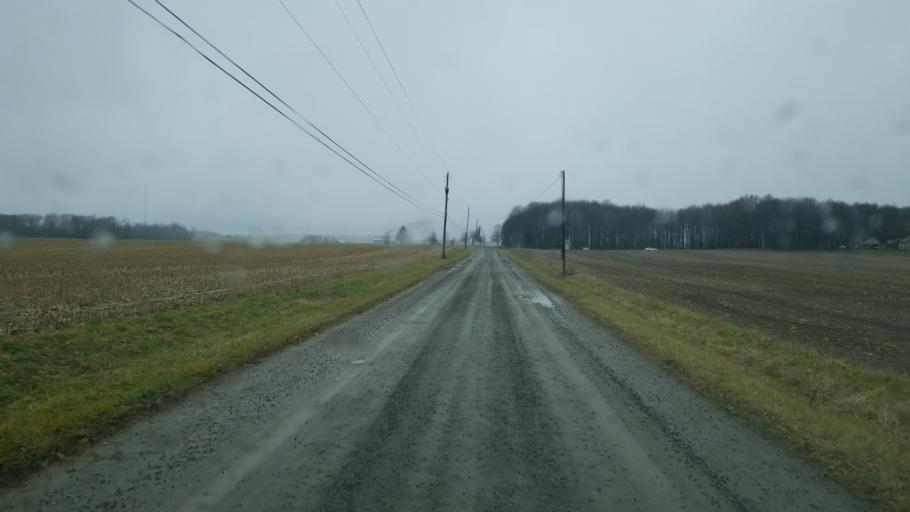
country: US
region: Ohio
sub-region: Ashtabula County
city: Roaming Shores
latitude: 41.5935
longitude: -80.7052
